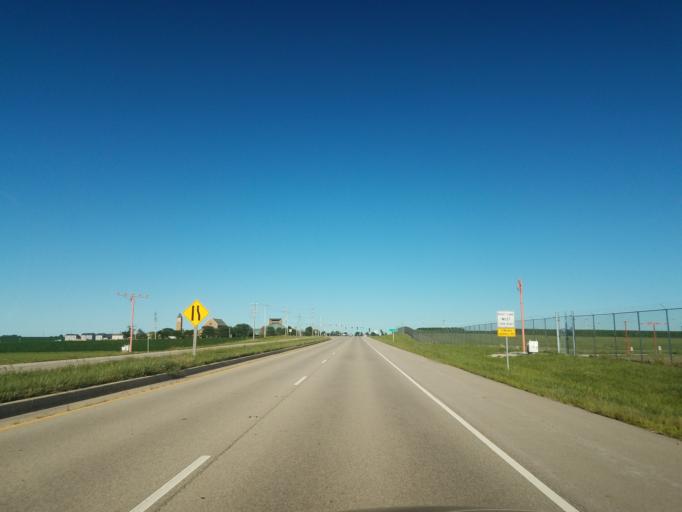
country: US
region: Illinois
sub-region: McLean County
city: Bloomington
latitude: 40.4881
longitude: -88.9065
